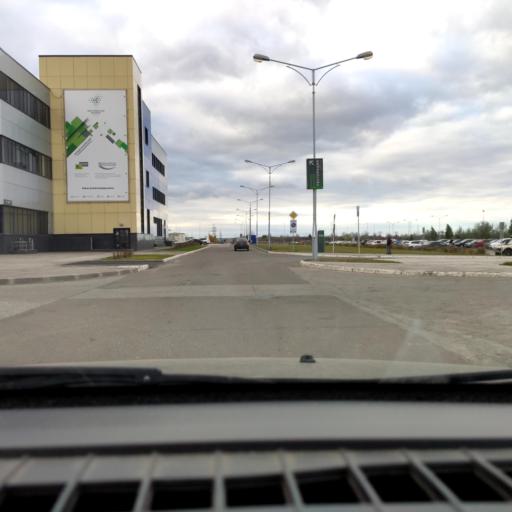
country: RU
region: Samara
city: Podstepki
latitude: 53.5575
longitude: 49.2145
